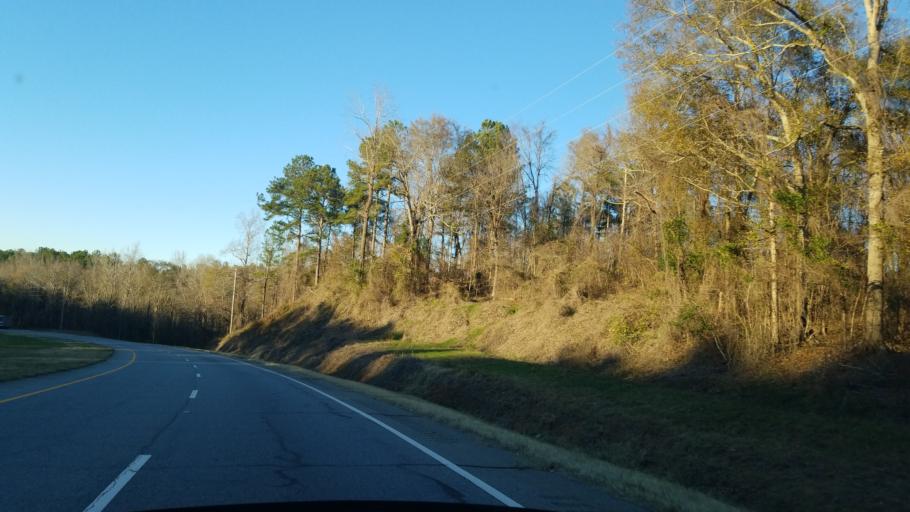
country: US
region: Georgia
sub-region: Chattahoochee County
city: Cusseta
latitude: 32.2395
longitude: -84.7139
